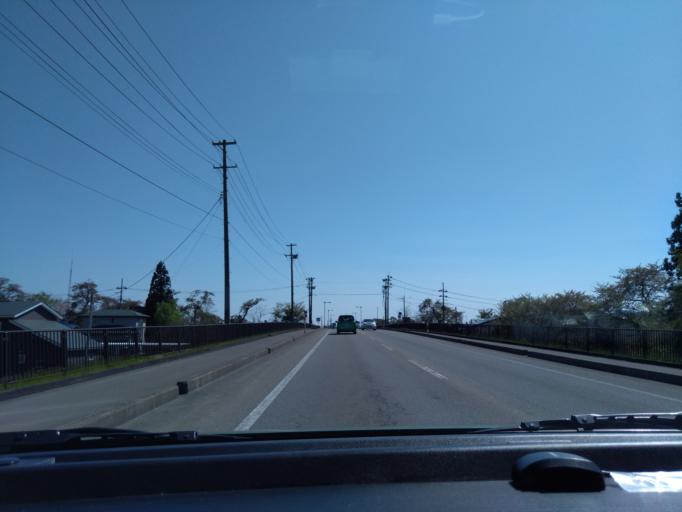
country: JP
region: Akita
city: Kakunodatemachi
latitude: 39.5821
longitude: 140.5690
